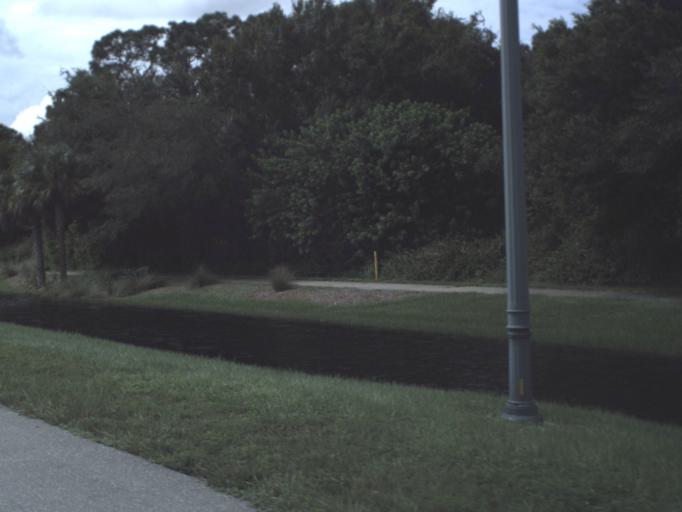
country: US
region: Florida
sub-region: Sarasota County
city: North Port
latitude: 27.0773
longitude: -82.1557
